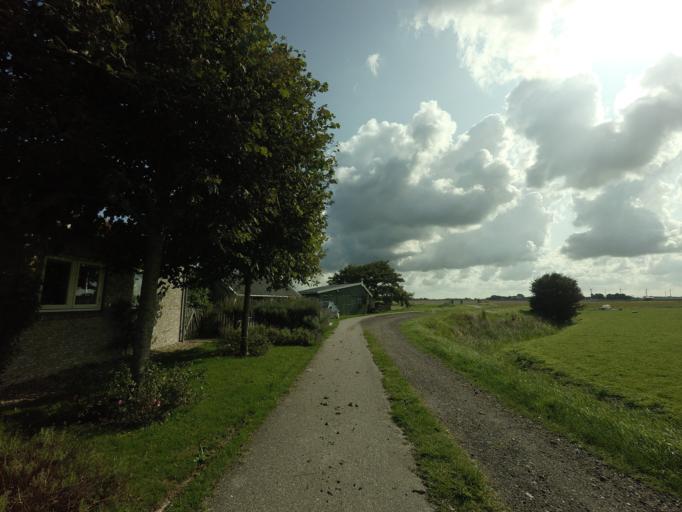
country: NL
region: Friesland
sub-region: Gemeente Franekeradeel
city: Tzummarum
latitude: 53.2621
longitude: 5.5494
